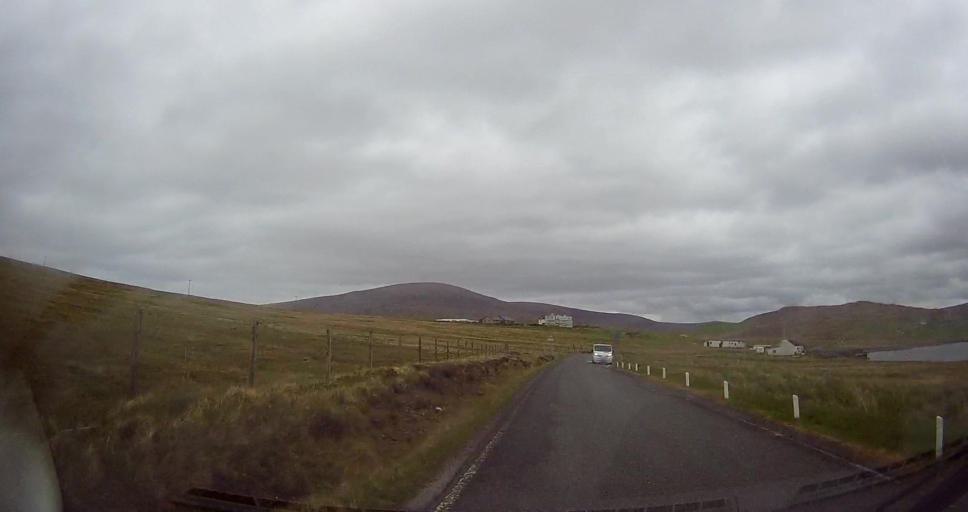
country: GB
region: Scotland
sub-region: Shetland Islands
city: Lerwick
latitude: 60.4882
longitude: -1.4666
